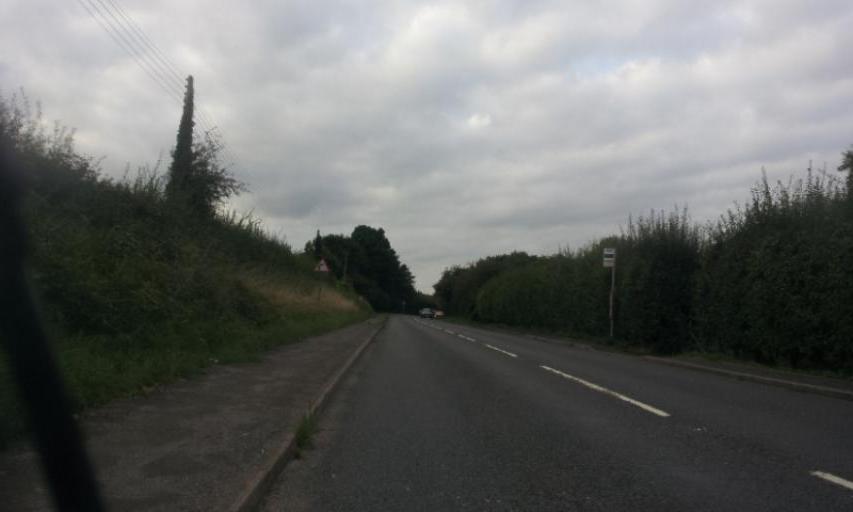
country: GB
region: England
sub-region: Kent
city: Wateringbury
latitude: 51.2434
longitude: 0.4110
